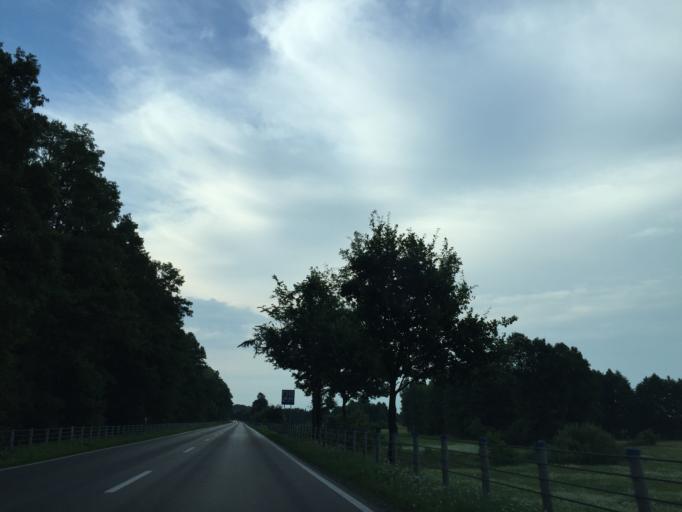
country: PL
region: Masovian Voivodeship
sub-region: Powiat ostrowski
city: Brok
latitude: 52.6843
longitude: 21.8516
